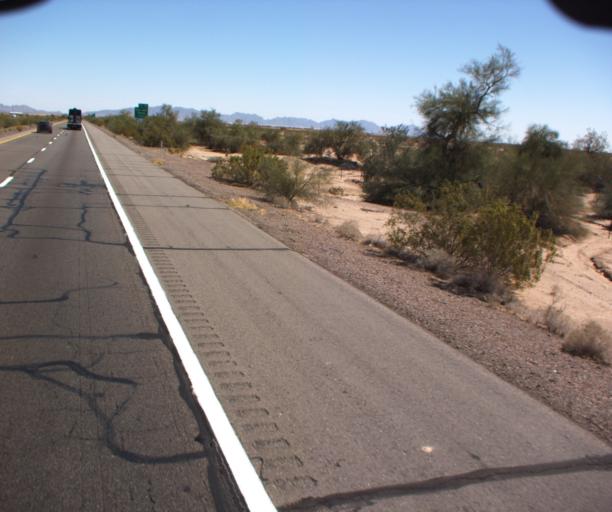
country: US
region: Arizona
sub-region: Yuma County
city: Wellton
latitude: 32.6898
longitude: -113.9764
